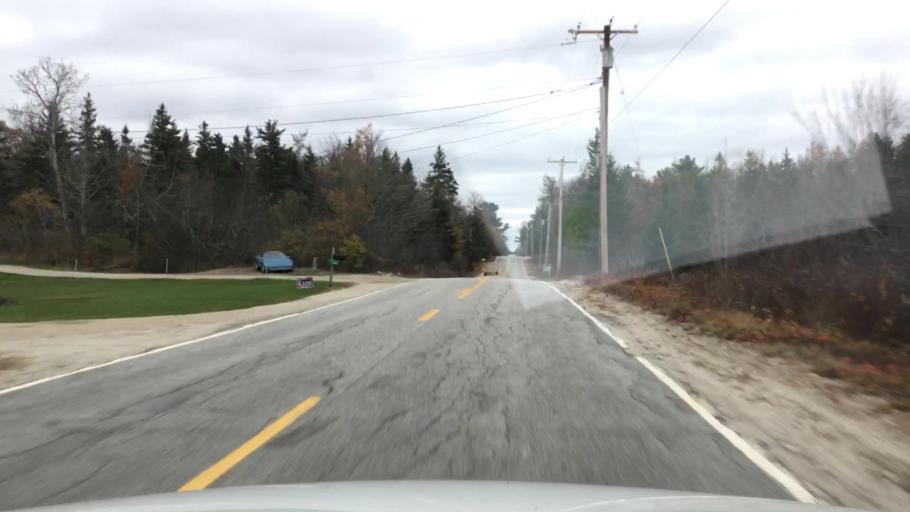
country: US
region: Maine
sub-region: Hancock County
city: Sedgwick
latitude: 44.3368
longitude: -68.5643
